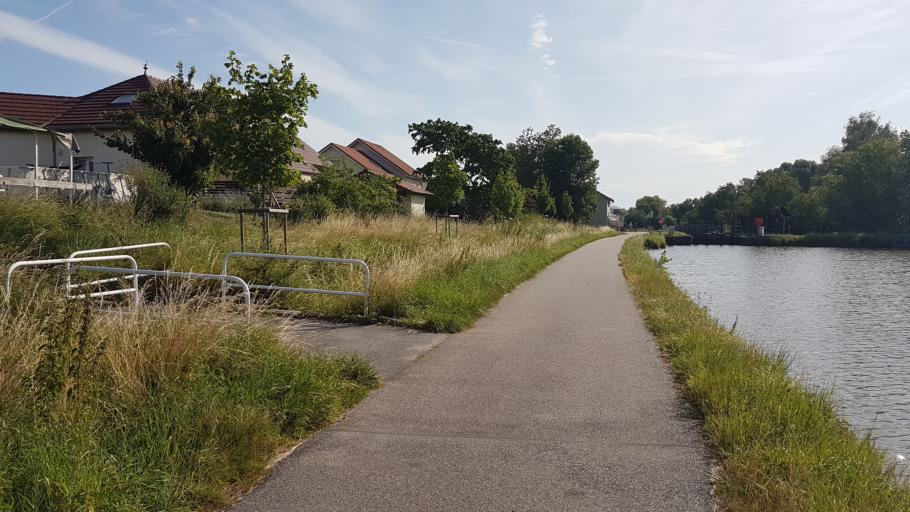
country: FR
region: Lorraine
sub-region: Departement des Vosges
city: Golbey
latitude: 48.1991
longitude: 6.4242
